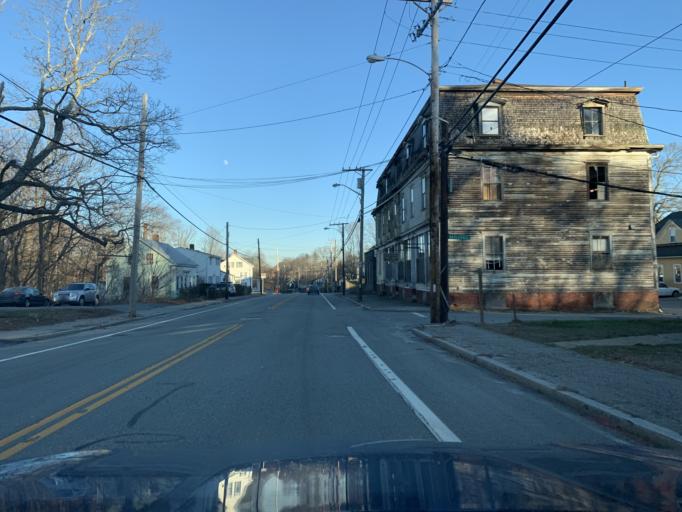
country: US
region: Rhode Island
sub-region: Kent County
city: West Warwick
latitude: 41.6947
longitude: -71.5519
